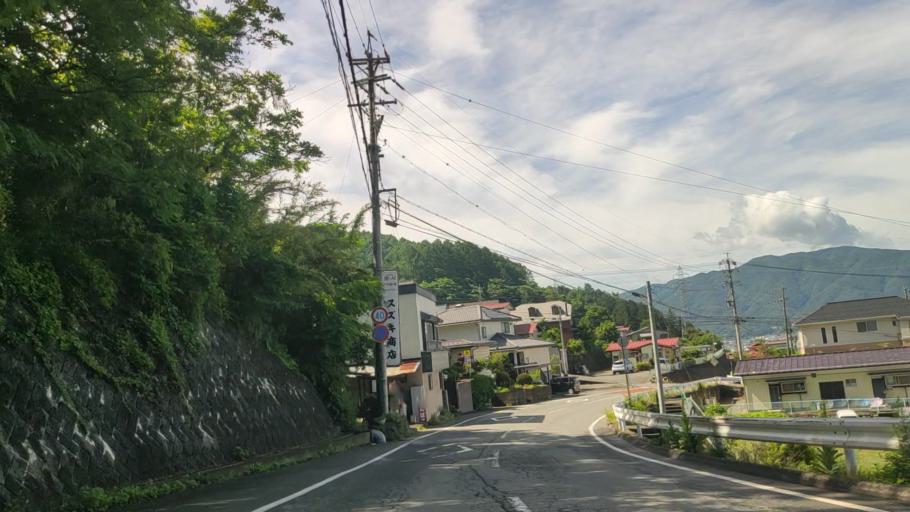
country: JP
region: Nagano
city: Suwa
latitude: 36.0475
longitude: 138.1282
